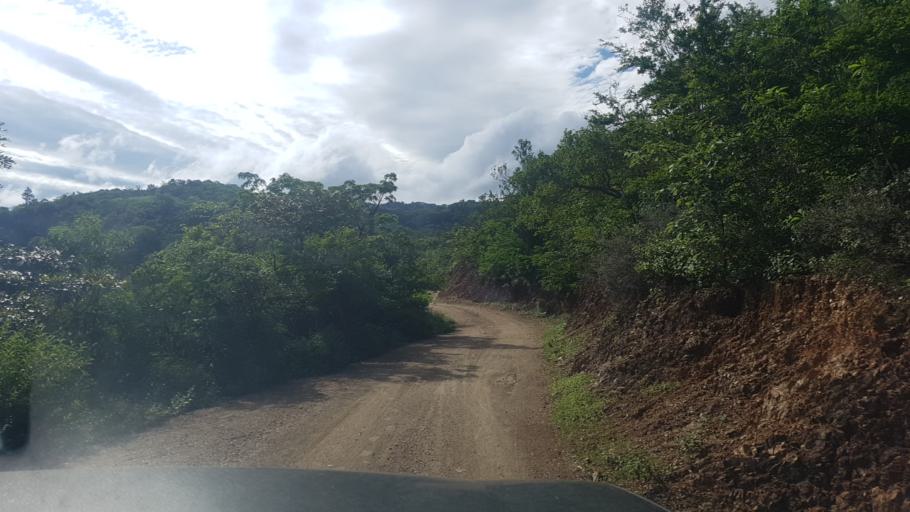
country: NI
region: Nueva Segovia
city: Ocotal
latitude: 13.6047
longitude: -86.4448
